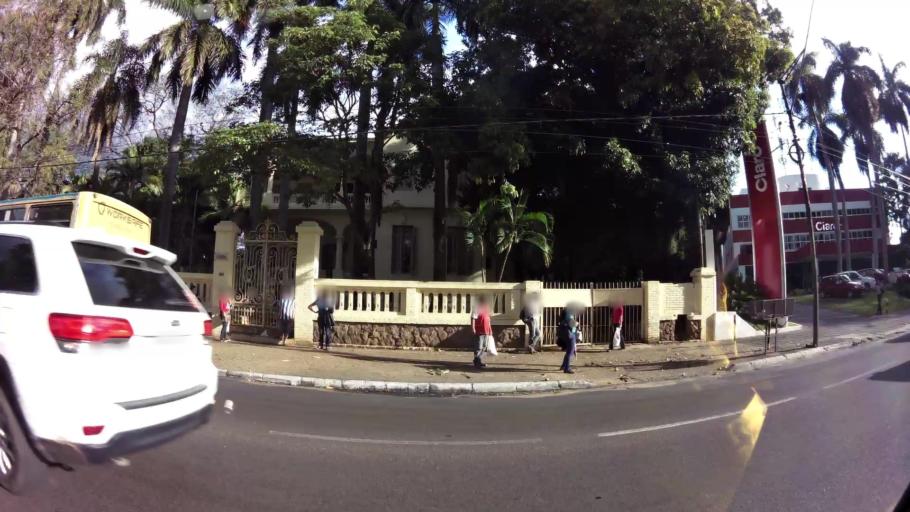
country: PY
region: Asuncion
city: Asuncion
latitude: -25.2928
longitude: -57.6047
